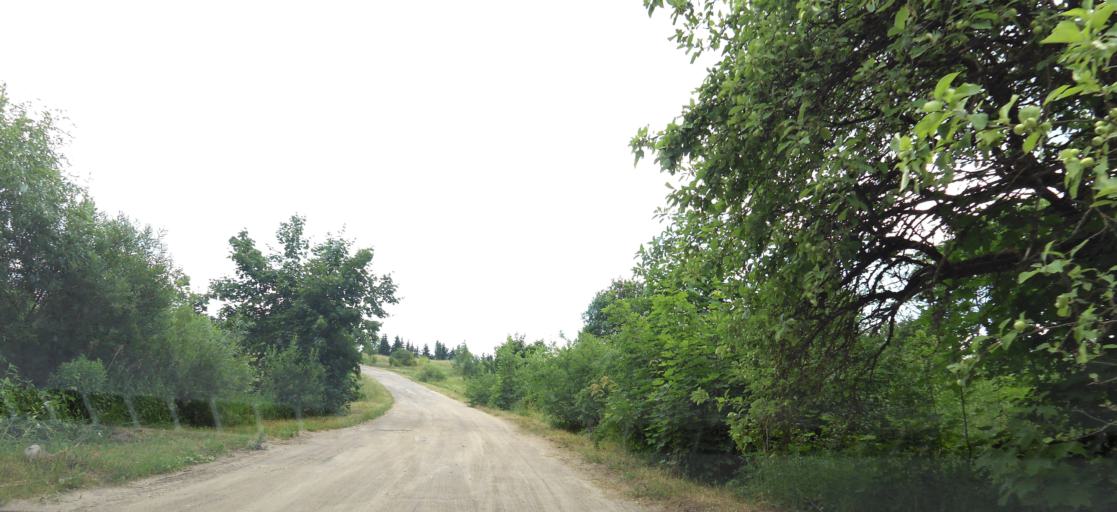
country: LT
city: Grigiskes
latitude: 54.7120
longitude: 25.0936
